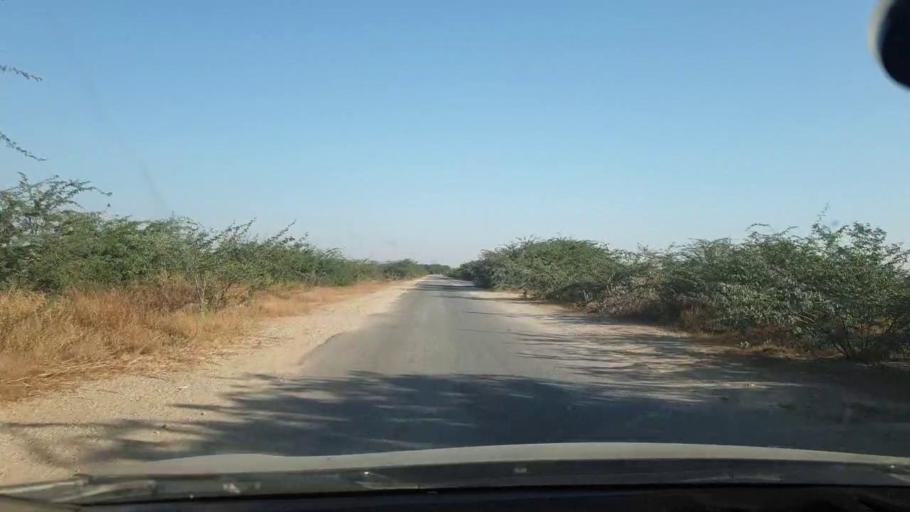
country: PK
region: Sindh
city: Malir Cantonment
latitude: 25.1647
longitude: 67.1960
